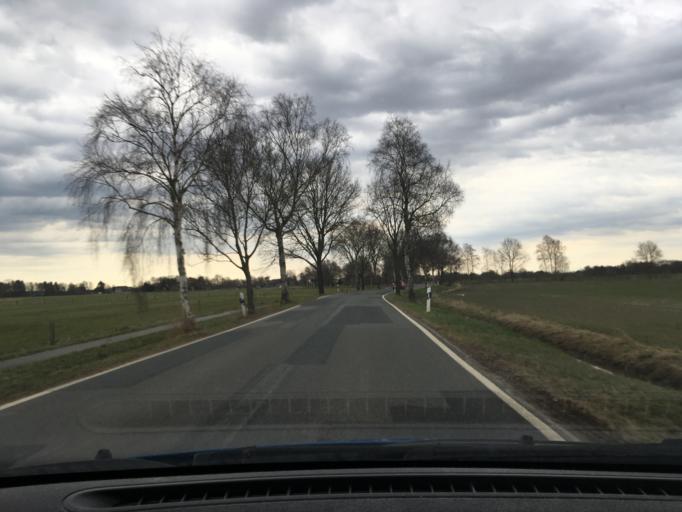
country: DE
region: Lower Saxony
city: Drage
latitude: 53.3747
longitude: 10.2747
